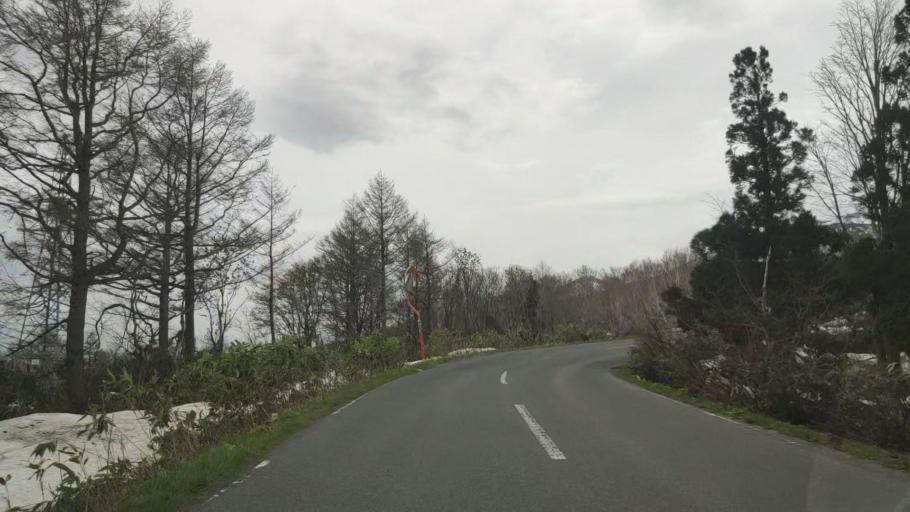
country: JP
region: Aomori
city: Aomori Shi
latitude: 40.7133
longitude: 140.8741
